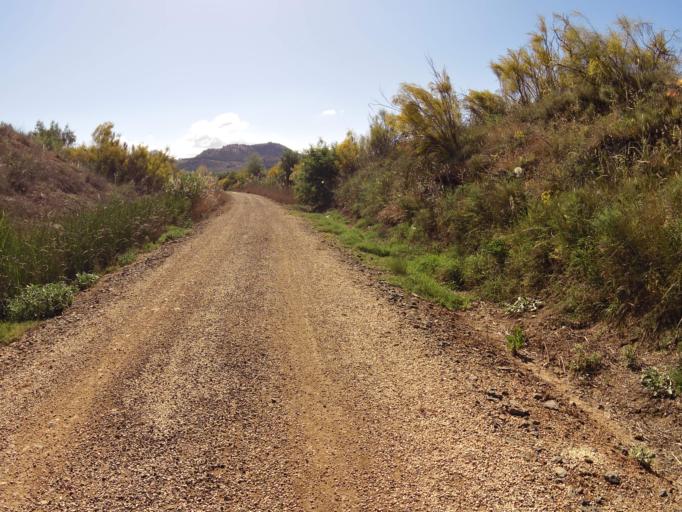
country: ES
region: Andalusia
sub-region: Provincia de Jaen
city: Alcaudete
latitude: 37.6033
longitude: -4.1499
